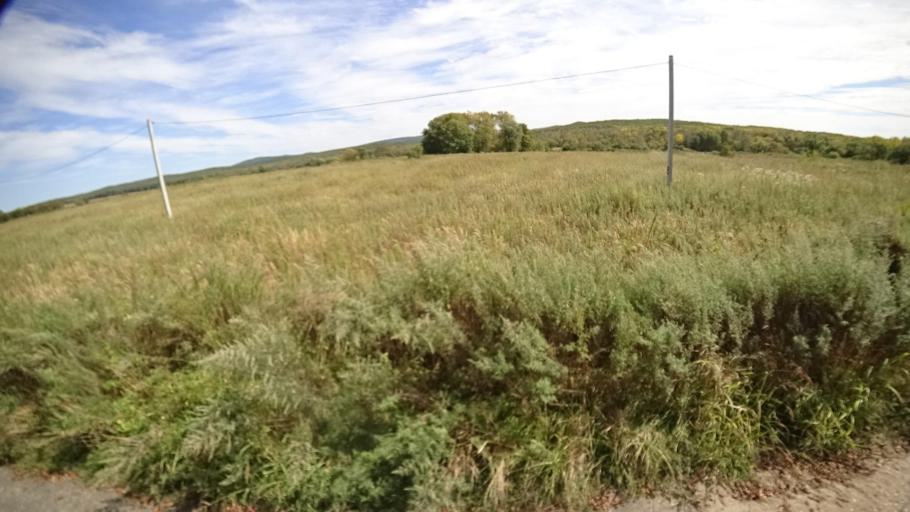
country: RU
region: Primorskiy
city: Yakovlevka
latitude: 44.6382
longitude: 133.5989
